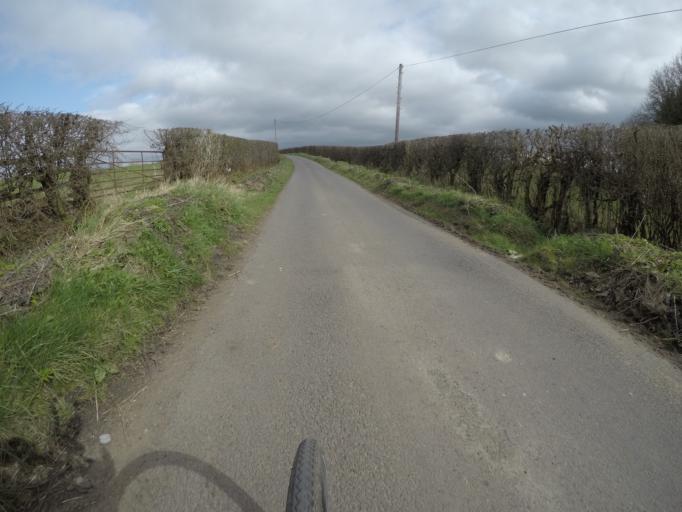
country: GB
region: Scotland
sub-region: North Ayrshire
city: Springside
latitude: 55.6437
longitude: -4.6240
